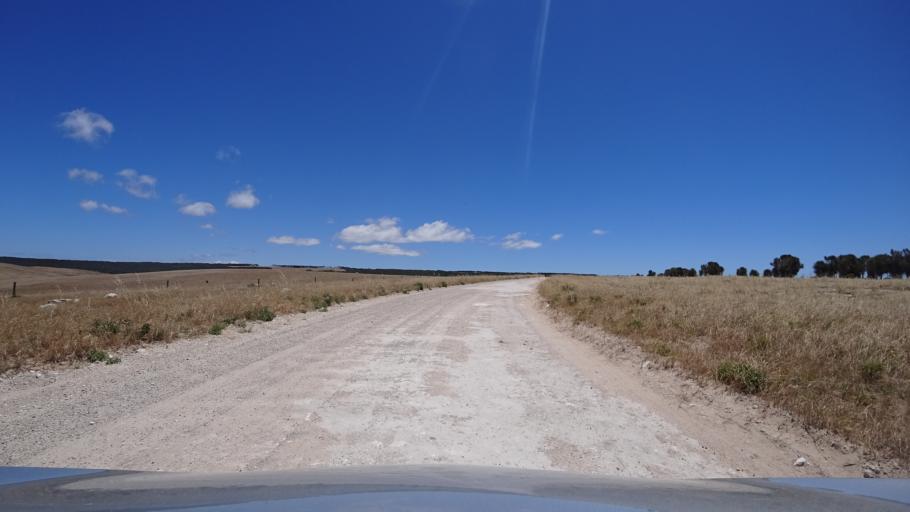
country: AU
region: South Australia
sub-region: Yankalilla
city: Normanville
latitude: -35.8423
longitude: 138.1275
